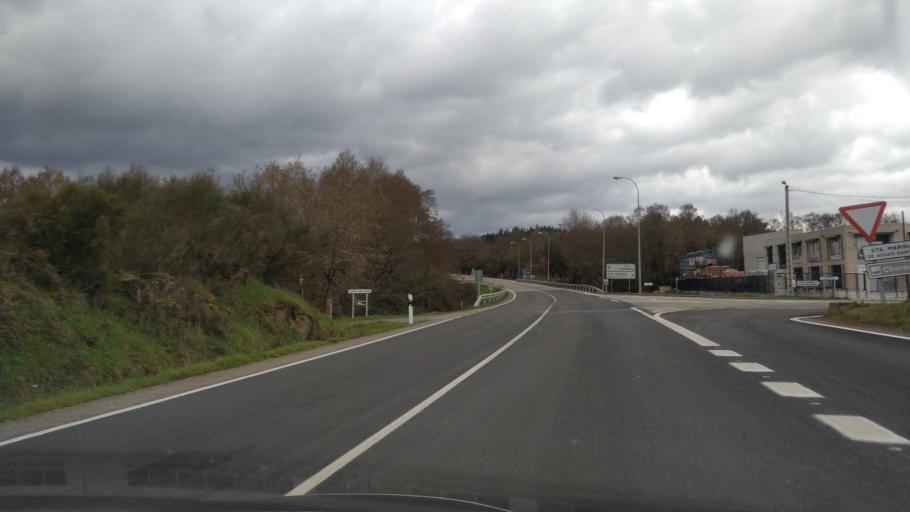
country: ES
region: Galicia
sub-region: Provincia de Ourense
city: Allariz
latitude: 42.1970
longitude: -7.7999
